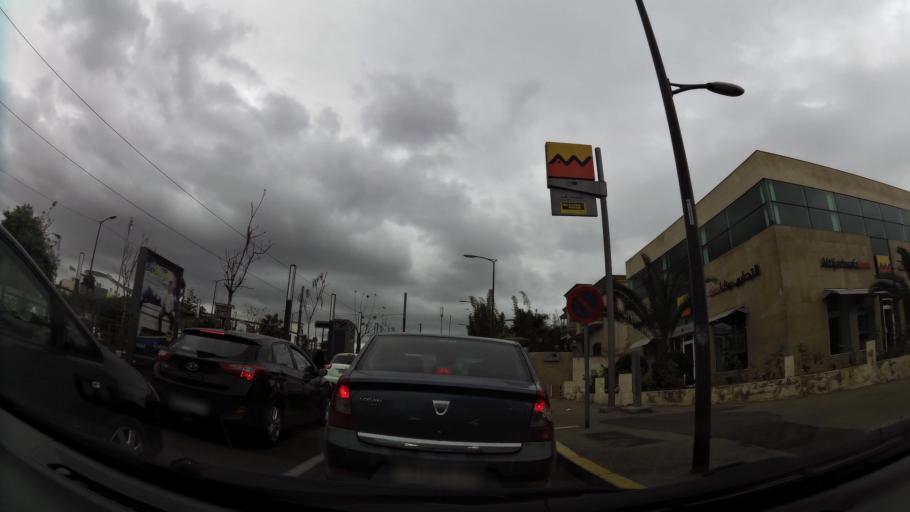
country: MA
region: Grand Casablanca
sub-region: Casablanca
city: Casablanca
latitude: 33.5475
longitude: -7.6320
